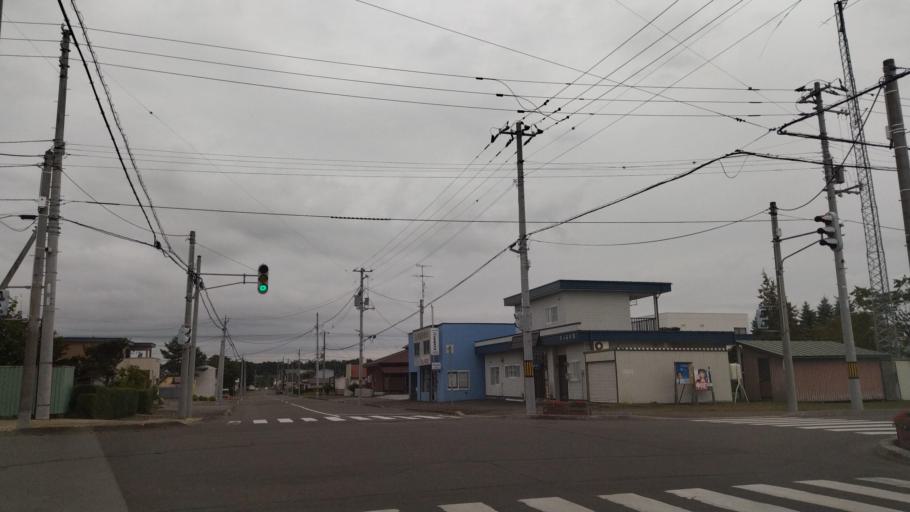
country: JP
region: Hokkaido
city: Otofuke
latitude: 43.2297
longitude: 143.2913
